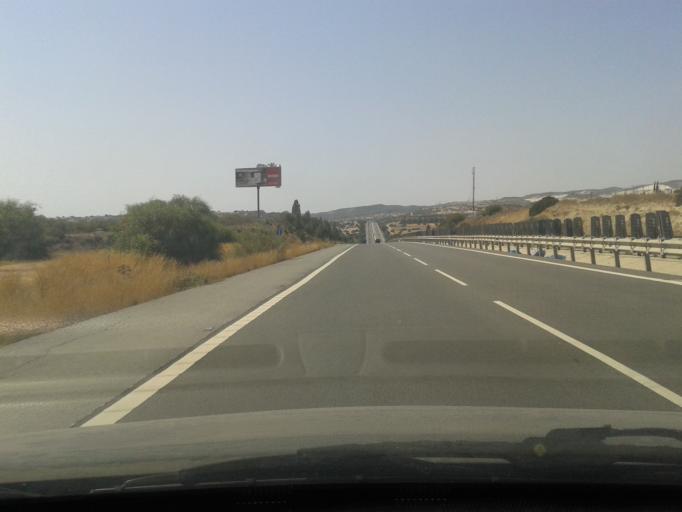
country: CY
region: Larnaka
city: Kofinou
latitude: 34.7537
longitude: 33.3137
